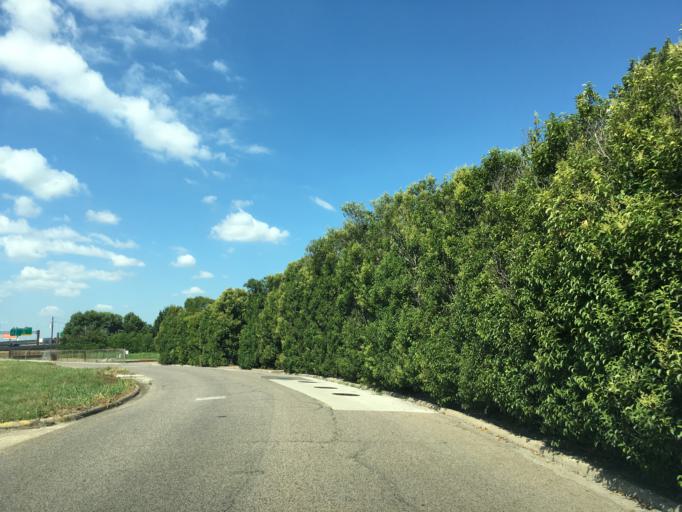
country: US
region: Texas
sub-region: Dallas County
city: Farmers Branch
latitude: 32.9143
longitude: -96.8765
